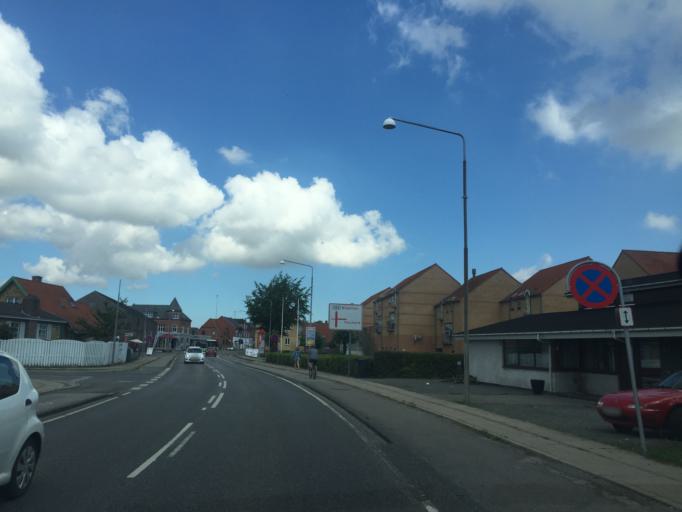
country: DK
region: South Denmark
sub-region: Nordfyns Kommune
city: Otterup
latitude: 55.5123
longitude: 10.3996
